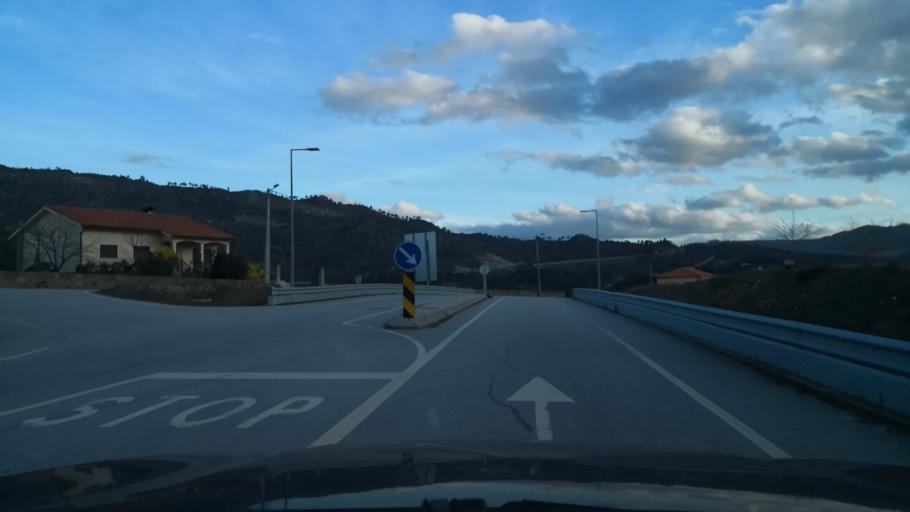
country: PT
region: Braganca
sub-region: Carrazeda de Ansiaes
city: Carrazeda de Anciaes
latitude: 41.3024
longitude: -7.3421
